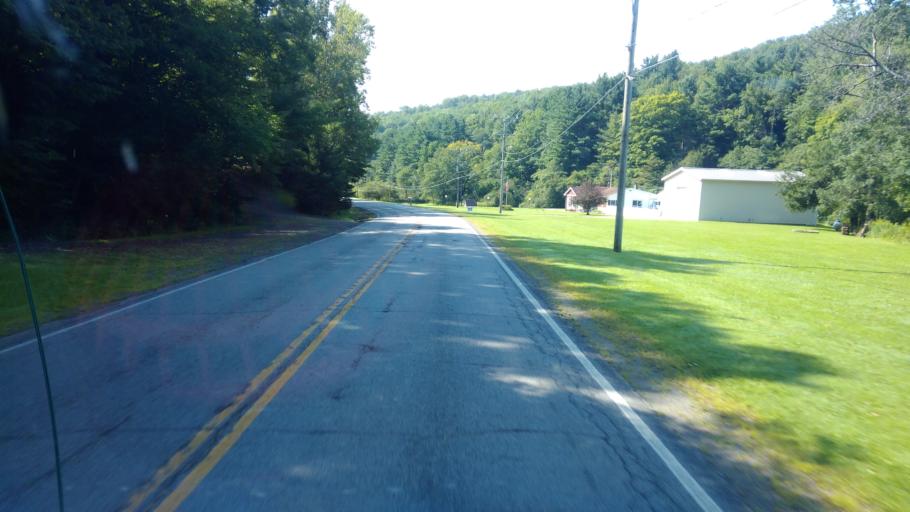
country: US
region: New York
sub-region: Allegany County
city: Bolivar
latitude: 42.1041
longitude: -78.1642
